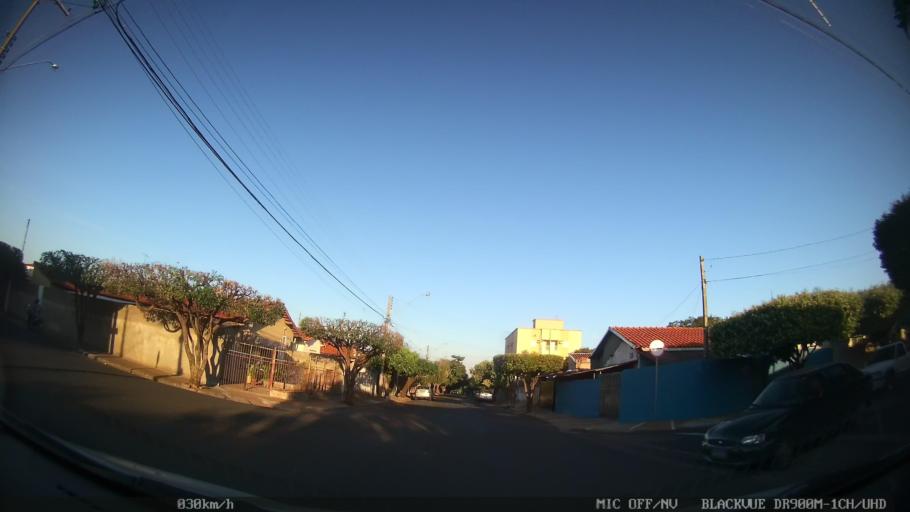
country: BR
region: Sao Paulo
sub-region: Sao Jose Do Rio Preto
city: Sao Jose do Rio Preto
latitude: -20.7974
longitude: -49.3846
